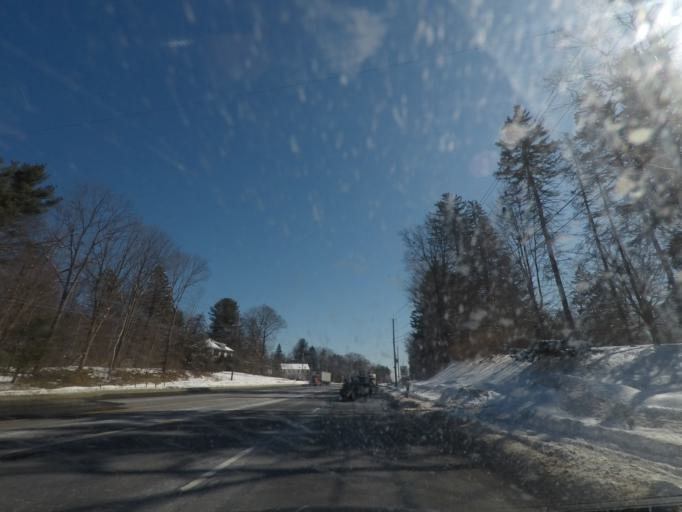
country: US
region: New York
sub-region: Schenectady County
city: Niskayuna
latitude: 42.7833
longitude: -73.8569
